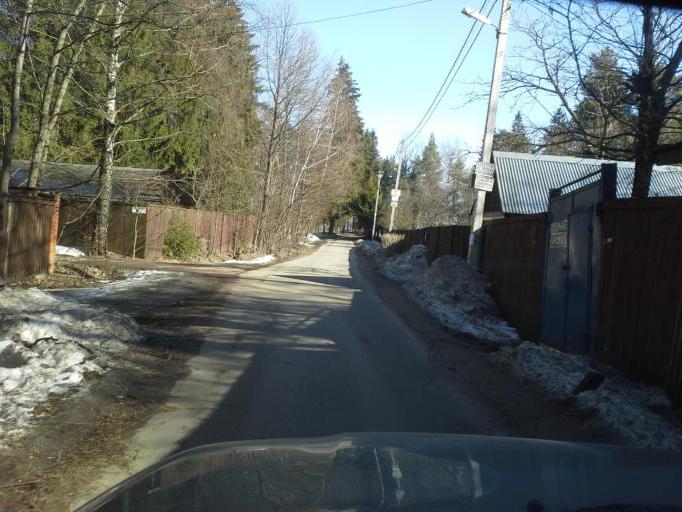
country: RU
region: Moskovskaya
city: Gorki Vtoryye
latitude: 55.6849
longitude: 37.1407
